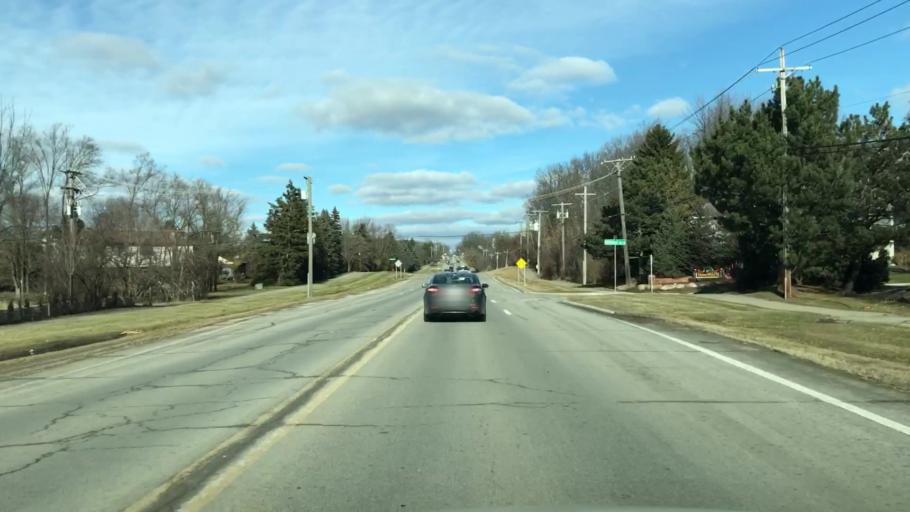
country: US
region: Michigan
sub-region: Oakland County
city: Auburn Hills
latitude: 42.7032
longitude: -83.1950
